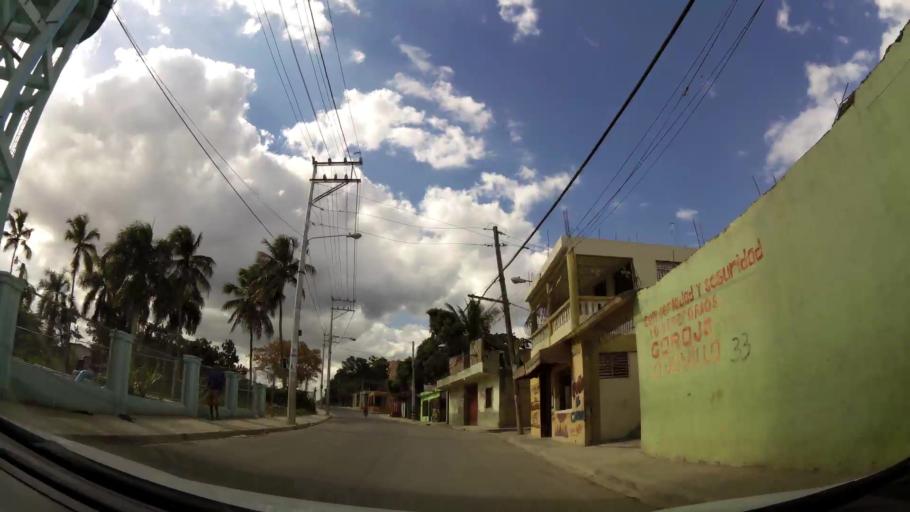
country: DO
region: Nacional
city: Ensanche Luperon
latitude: 18.5413
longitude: -69.8856
